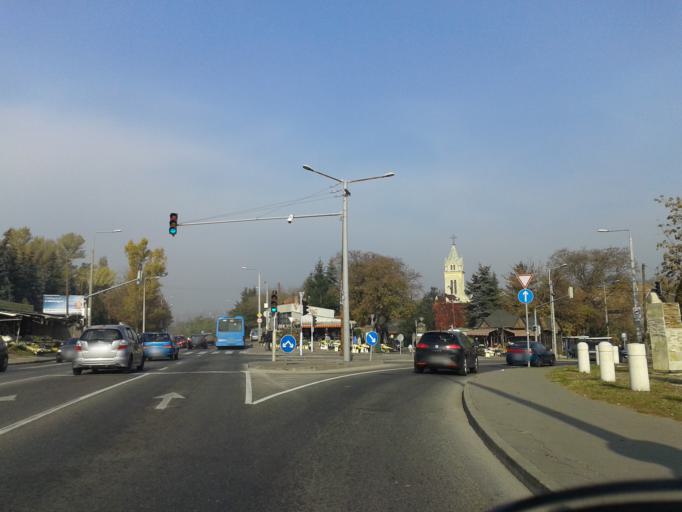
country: HU
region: Pest
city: Urom
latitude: 47.5650
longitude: 19.0225
